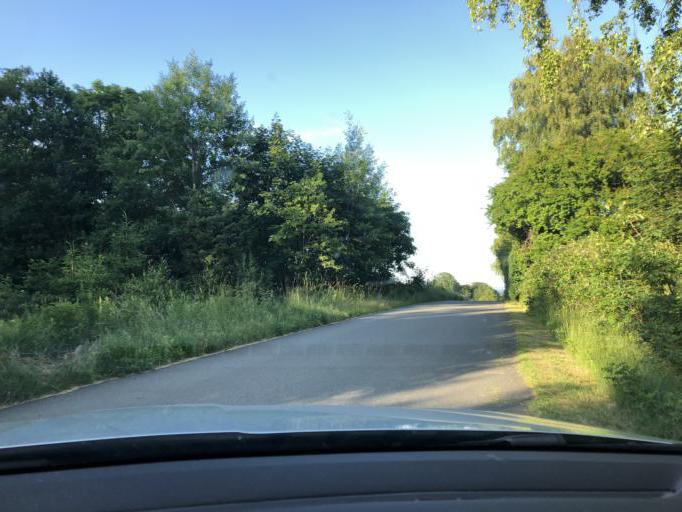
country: SE
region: Blekinge
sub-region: Solvesborgs Kommun
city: Soelvesborg
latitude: 56.1424
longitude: 14.5963
